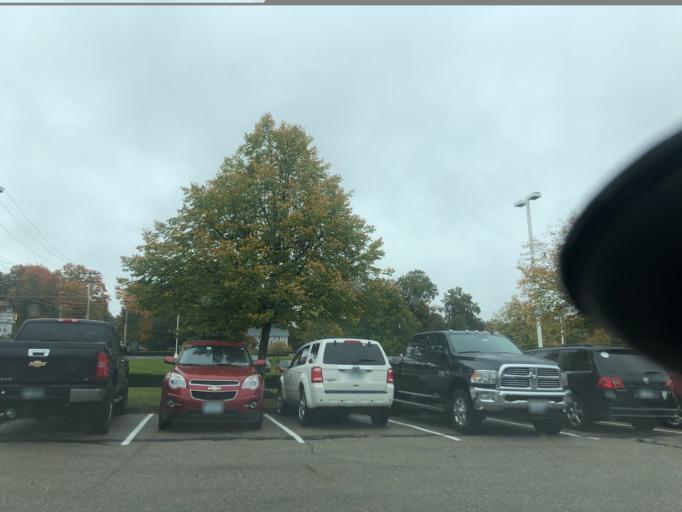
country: US
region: New Hampshire
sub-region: Strafford County
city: Dover
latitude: 43.2066
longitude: -70.8673
